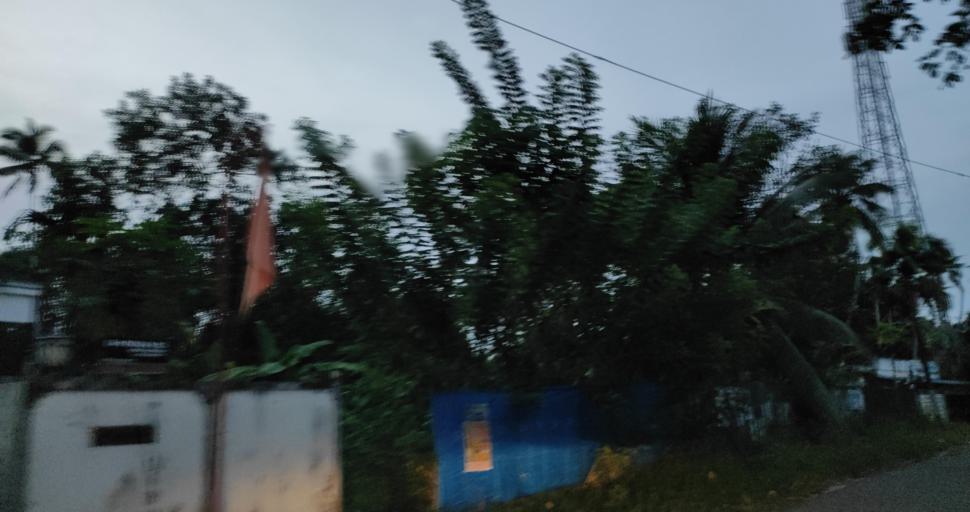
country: IN
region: Kerala
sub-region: Alappuzha
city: Vayalar
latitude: 9.6983
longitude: 76.3134
